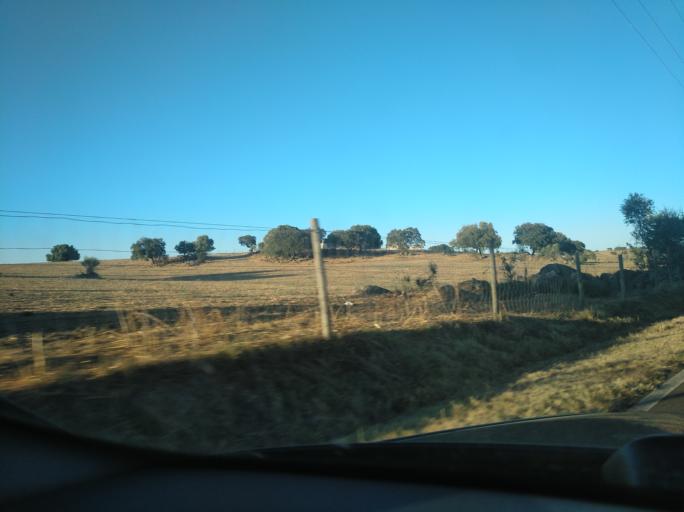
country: PT
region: Portalegre
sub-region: Arronches
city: Arronches
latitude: 39.0688
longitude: -7.2057
